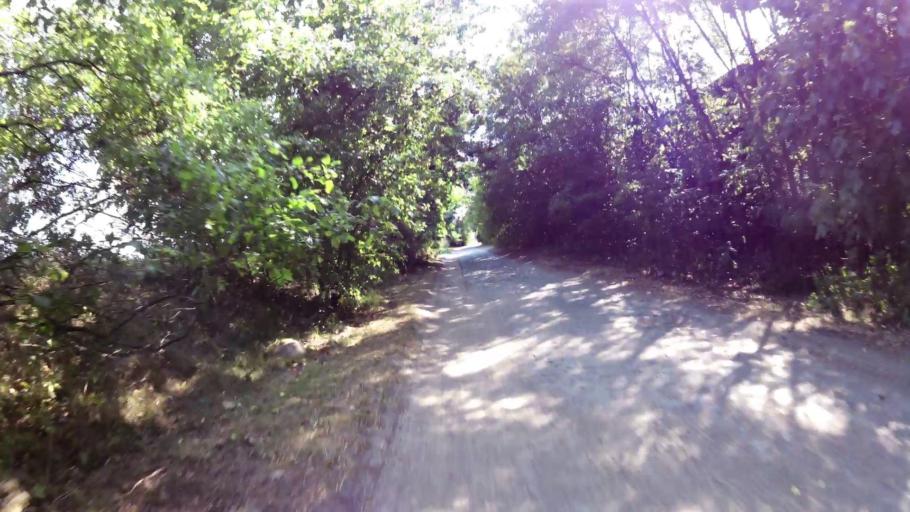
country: PL
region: West Pomeranian Voivodeship
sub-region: Powiat gryfinski
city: Moryn
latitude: 52.8598
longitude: 14.4237
